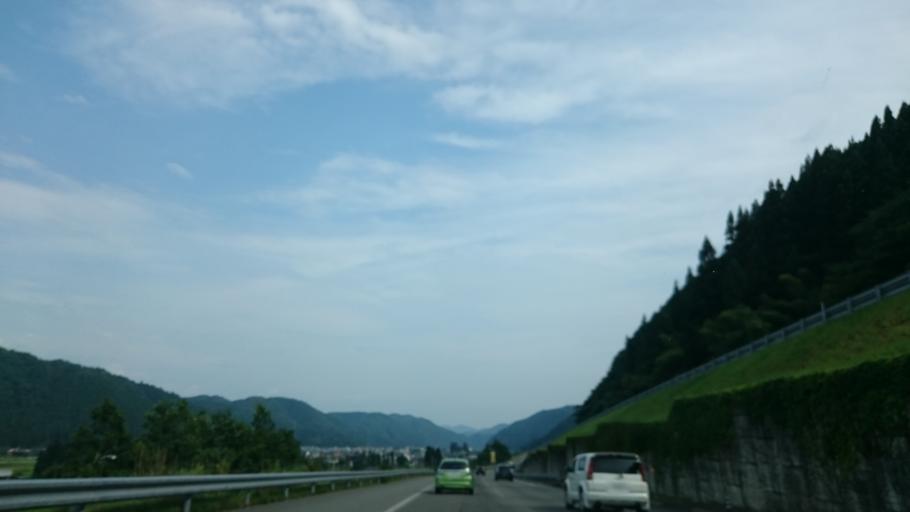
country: JP
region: Gifu
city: Gujo
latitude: 35.8286
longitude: 136.8824
